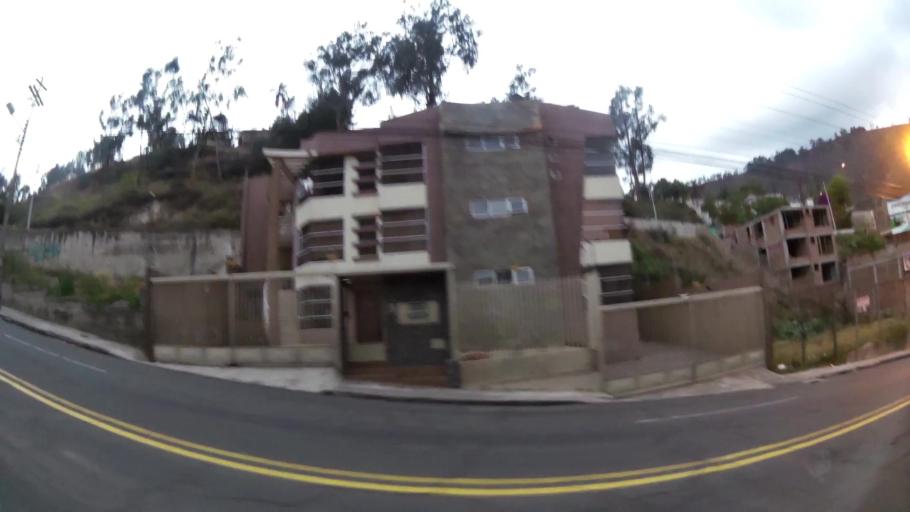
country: EC
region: Tungurahua
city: Ambato
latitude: -1.2555
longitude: -78.6441
